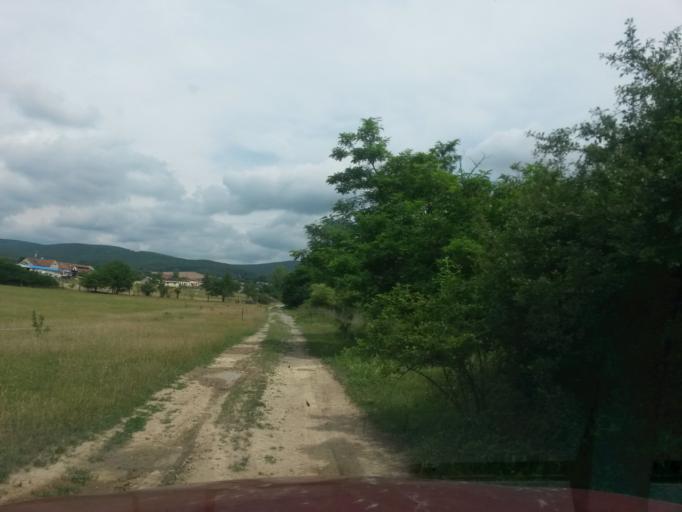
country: SK
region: Kosicky
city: Moldava nad Bodvou
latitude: 48.6669
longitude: 21.1123
